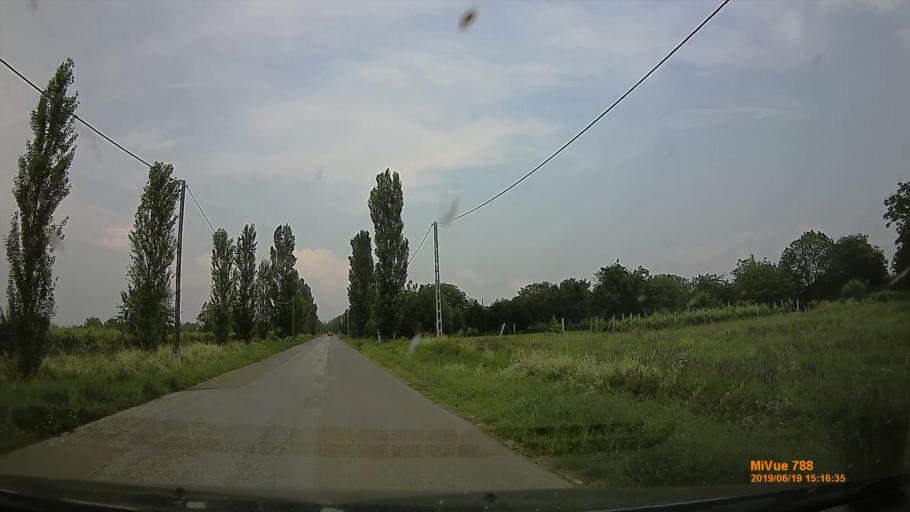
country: HU
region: Baranya
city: Szigetvar
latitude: 46.0781
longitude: 17.8417
